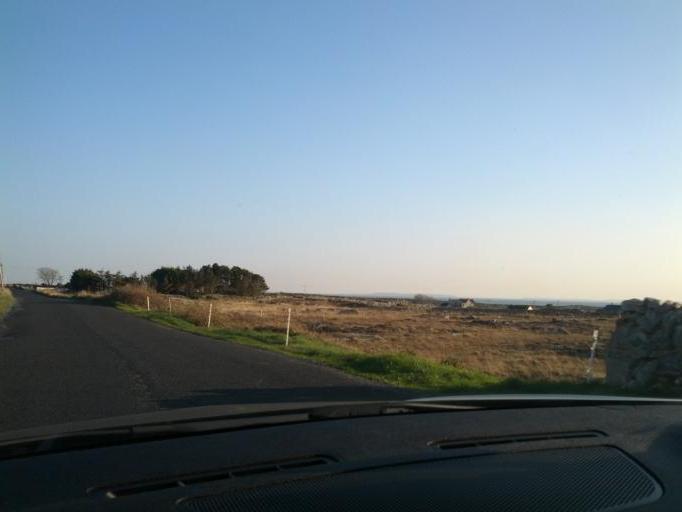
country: IE
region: Connaught
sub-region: County Galway
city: Oughterard
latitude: 53.2514
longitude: -9.5414
